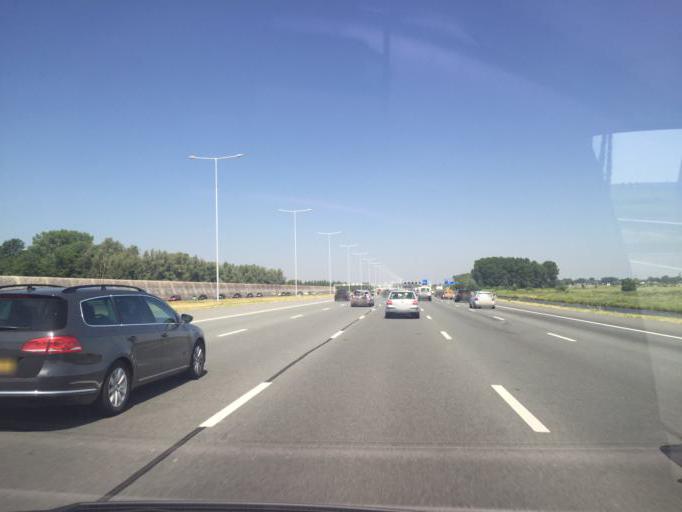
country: NL
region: North Holland
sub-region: Gemeente Amsterdam
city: Amsterdam-Zuidoost
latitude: 52.2485
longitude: 4.9700
